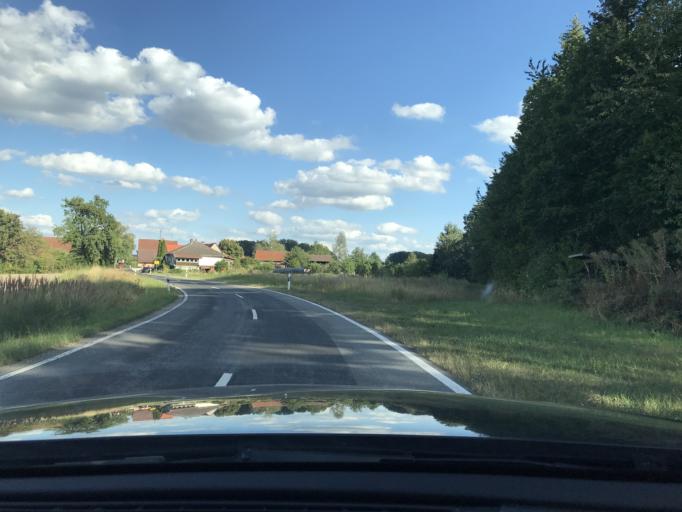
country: DE
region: Bavaria
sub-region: Regierungsbezirk Unterfranken
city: Burgpreppach
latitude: 50.0771
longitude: 10.6569
